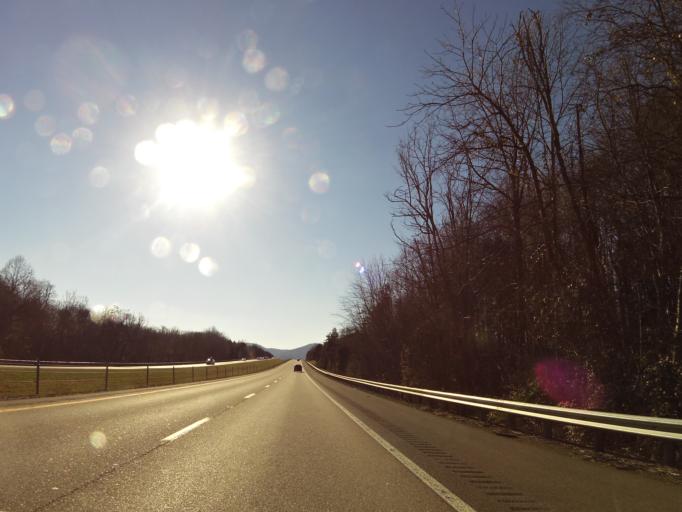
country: US
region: Tennessee
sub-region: Jefferson County
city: White Pine
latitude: 36.0126
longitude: -83.2943
